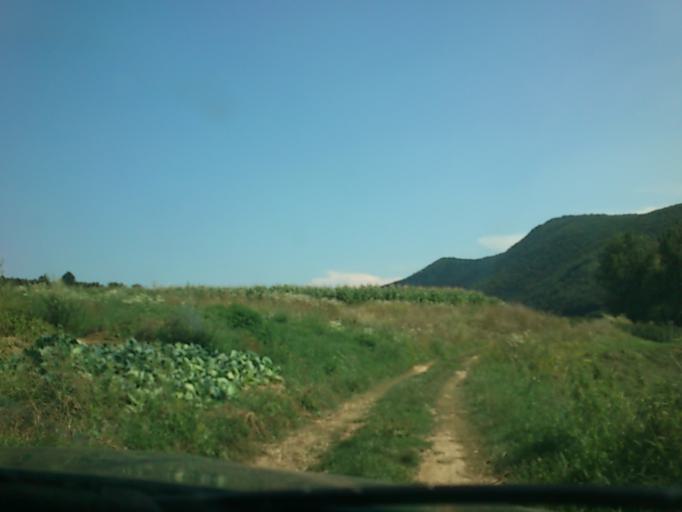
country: HR
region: Licko-Senjska
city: Otocac
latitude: 44.8724
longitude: 15.1824
